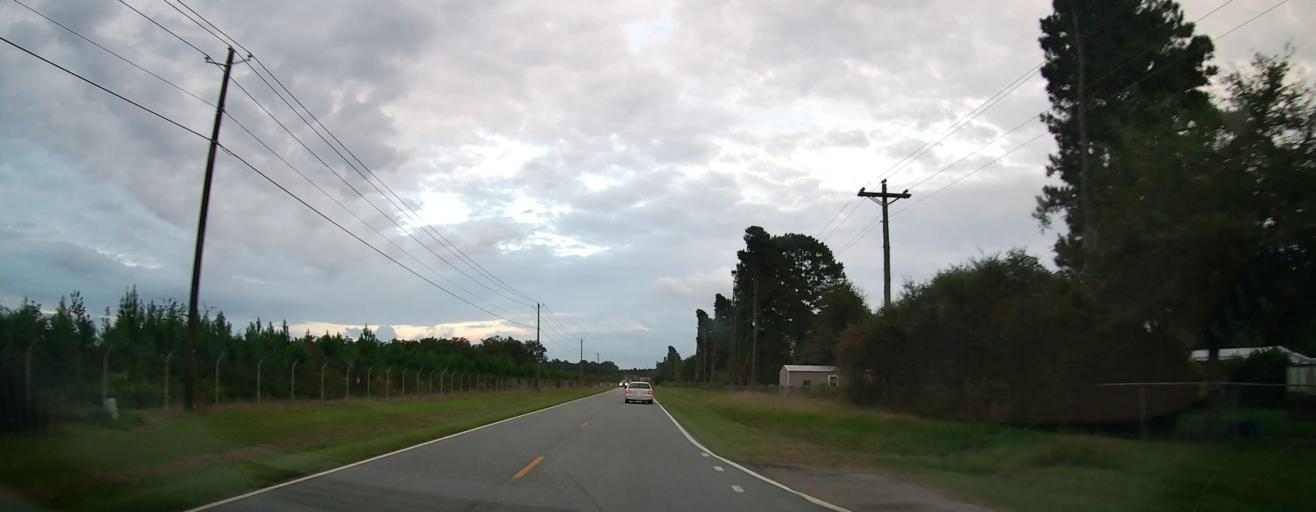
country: US
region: Georgia
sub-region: Houston County
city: Centerville
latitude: 32.6514
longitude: -83.7183
